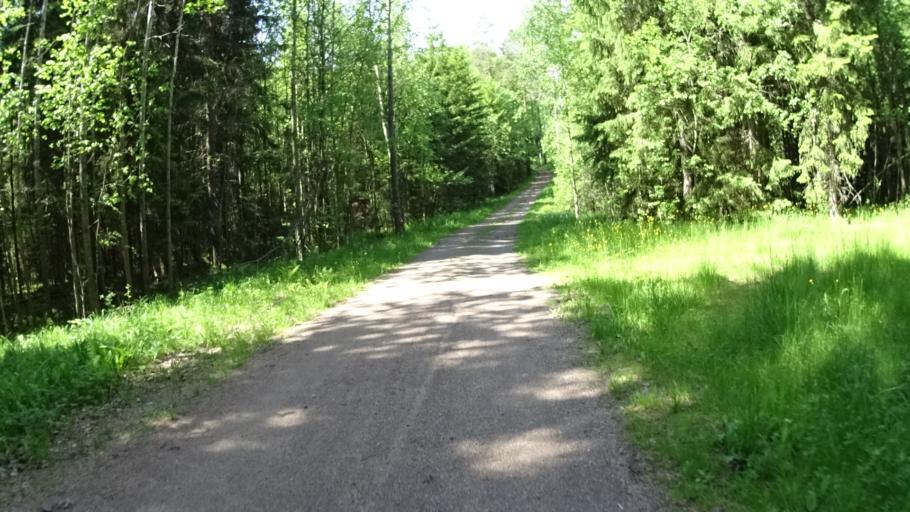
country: FI
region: Uusimaa
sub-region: Helsinki
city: Kilo
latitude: 60.3239
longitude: 24.7615
